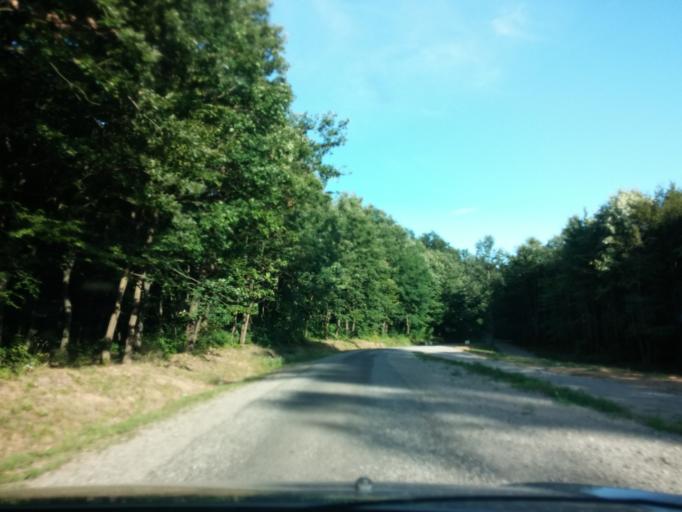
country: HU
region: Somogy
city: Kaposmero
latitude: 46.2495
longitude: 17.7557
